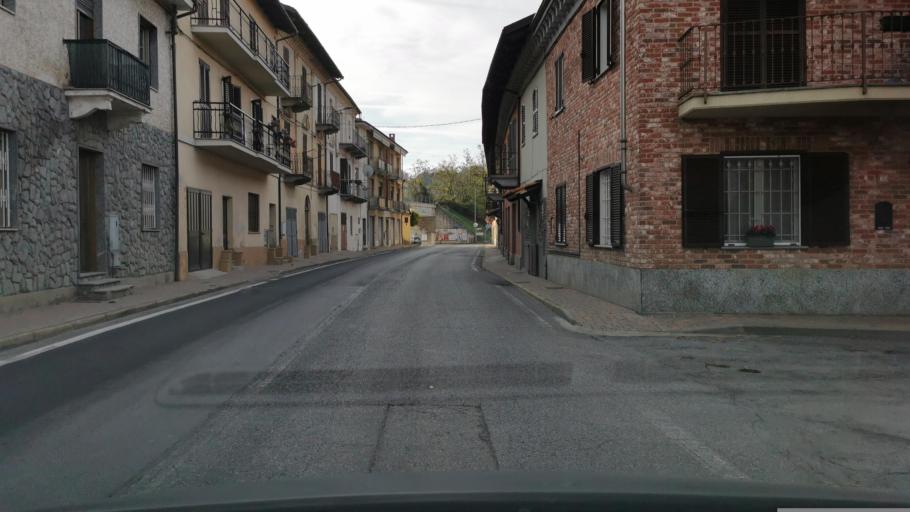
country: IT
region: Piedmont
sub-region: Provincia di Cuneo
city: Monchiero Borgonuovo
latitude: 44.5701
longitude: 7.9174
